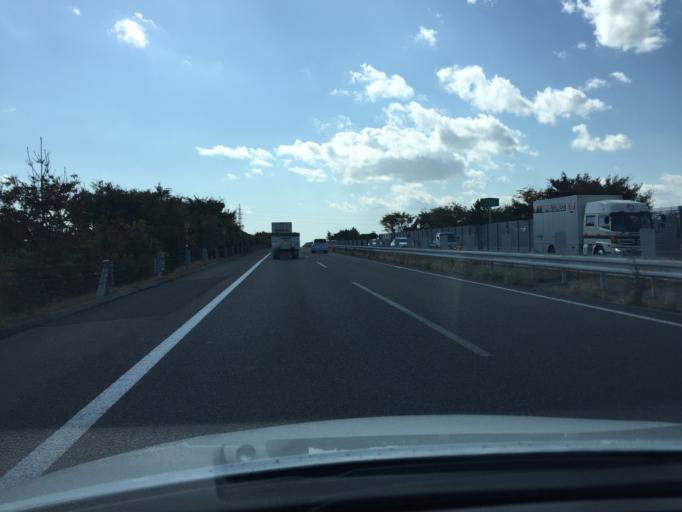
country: JP
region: Fukushima
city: Koriyama
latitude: 37.4479
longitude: 140.3527
